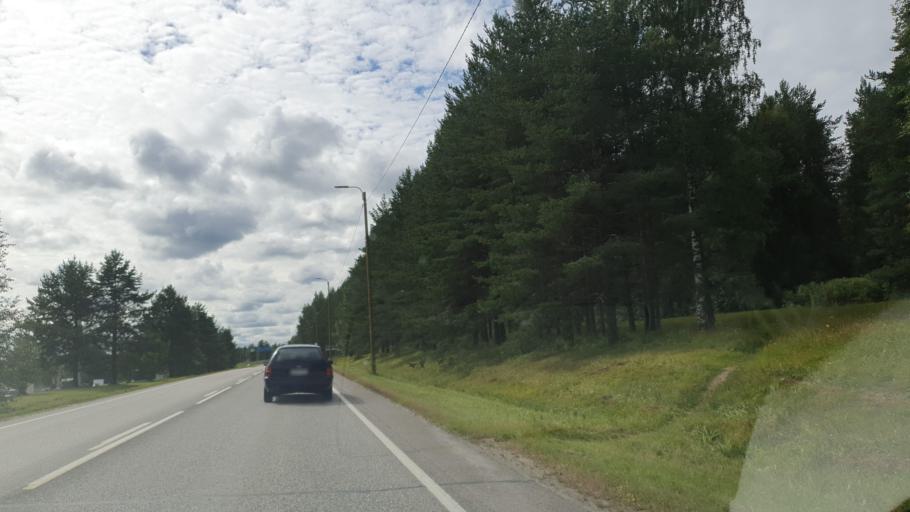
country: FI
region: Kainuu
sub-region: Kajaani
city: Kajaani
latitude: 64.2166
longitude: 27.6747
